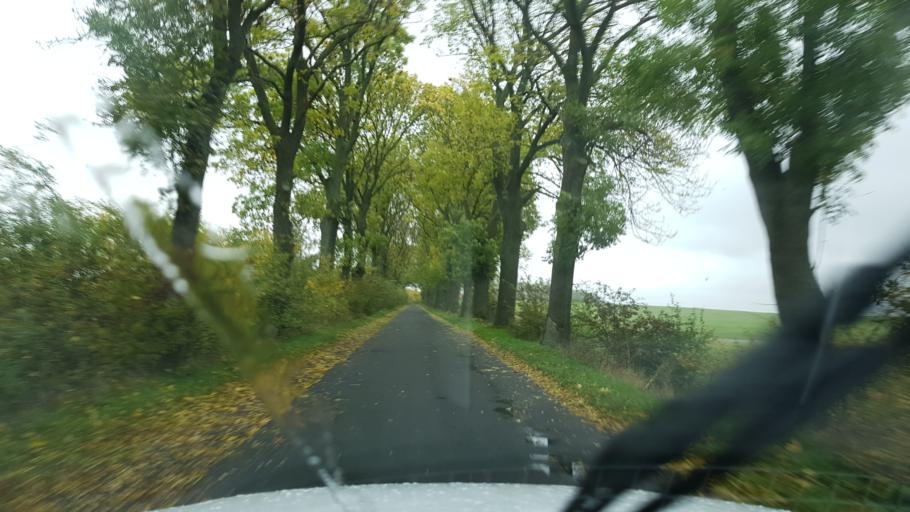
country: PL
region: West Pomeranian Voivodeship
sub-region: Powiat pyrzycki
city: Kozielice
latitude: 53.0592
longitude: 14.8775
